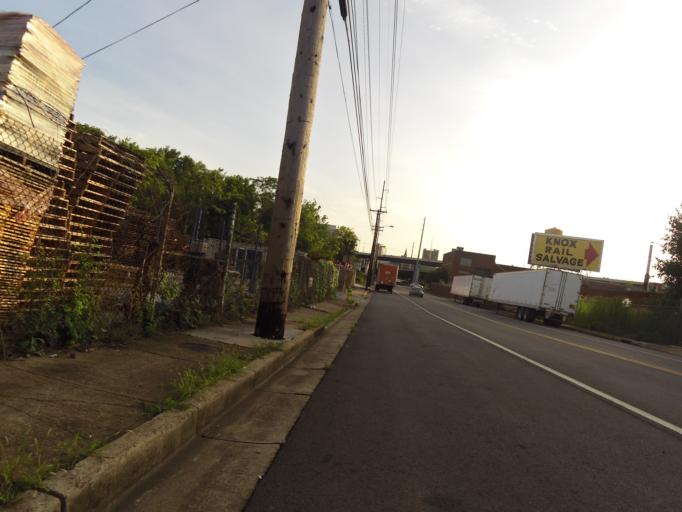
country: US
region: Tennessee
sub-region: Knox County
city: Knoxville
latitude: 35.9721
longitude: -83.9134
